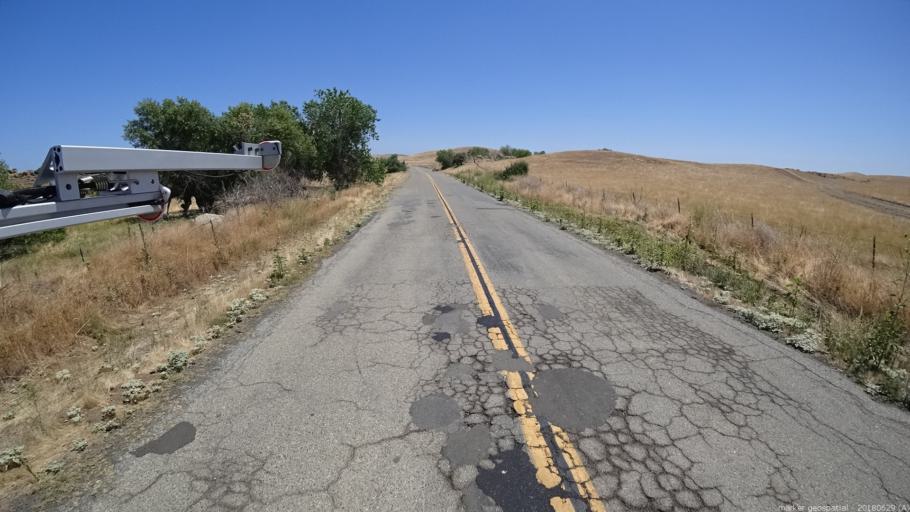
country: US
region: California
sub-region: Madera County
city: Bonadelle Ranchos-Madera Ranchos
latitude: 37.0787
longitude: -119.8906
